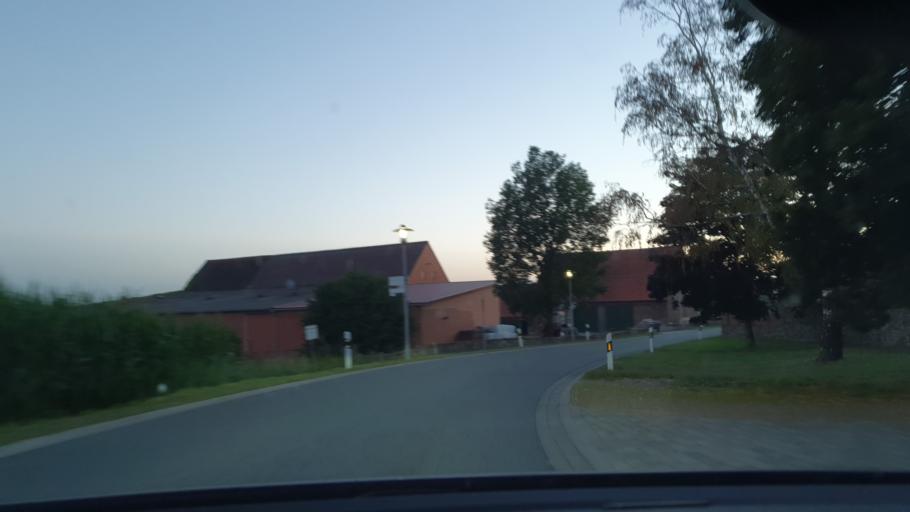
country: DE
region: North Rhine-Westphalia
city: Spenge
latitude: 52.1641
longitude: 8.4703
